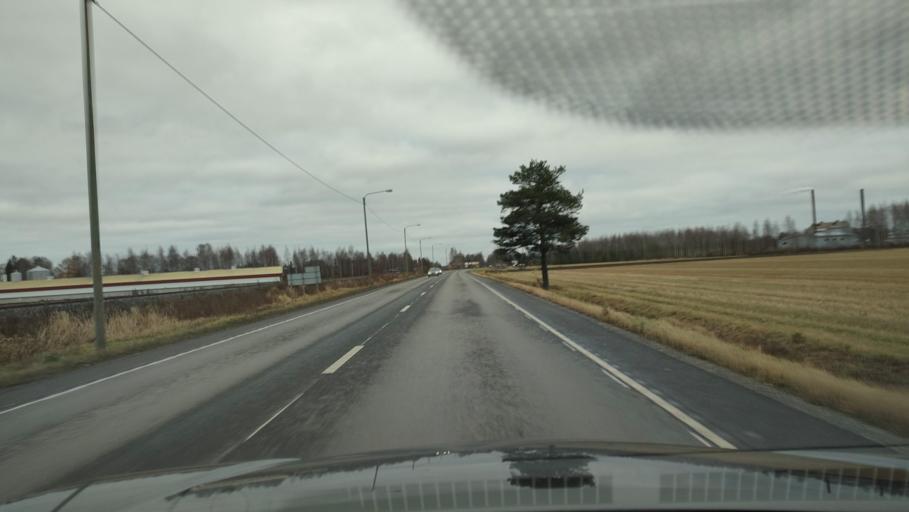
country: FI
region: Southern Ostrobothnia
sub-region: Seinaejoki
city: Ilmajoki
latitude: 62.7231
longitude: 22.5718
